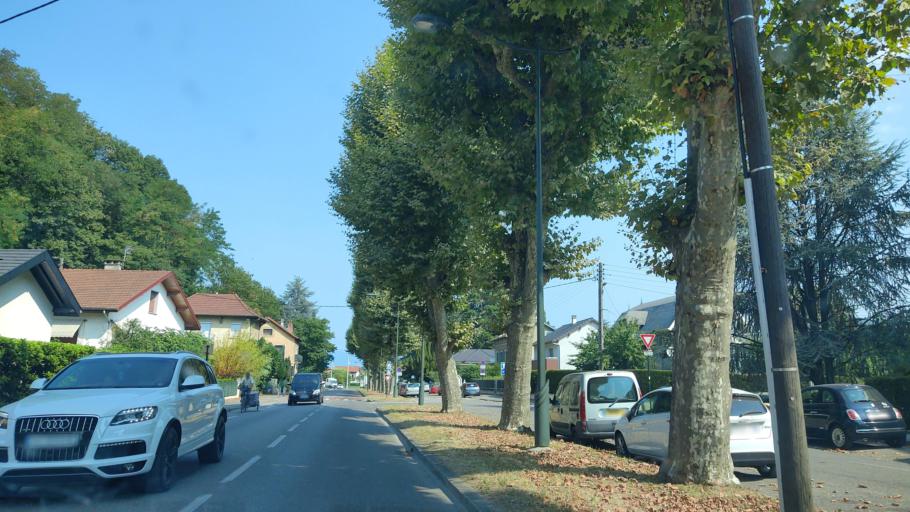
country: FR
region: Rhone-Alpes
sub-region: Departement de la Savoie
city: Tresserve
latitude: 45.6922
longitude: 5.9017
